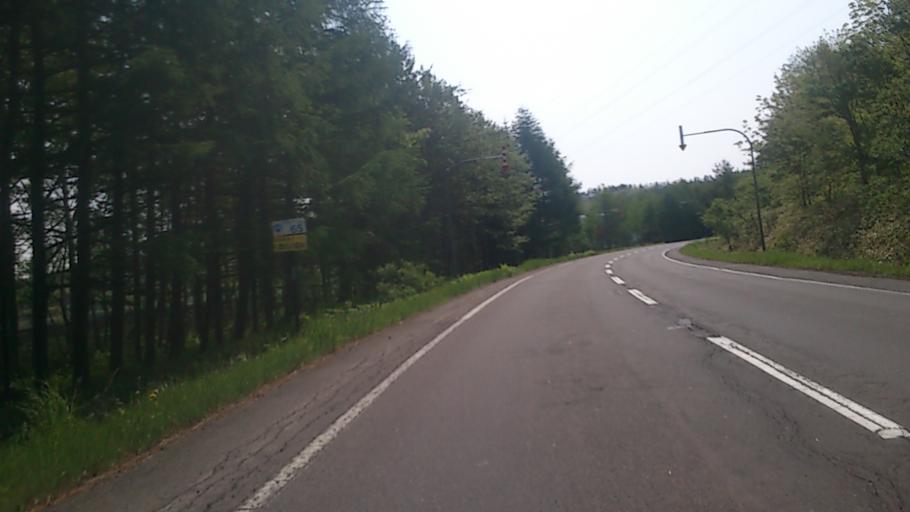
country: JP
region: Hokkaido
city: Kushiro
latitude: 43.4840
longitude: 144.5335
